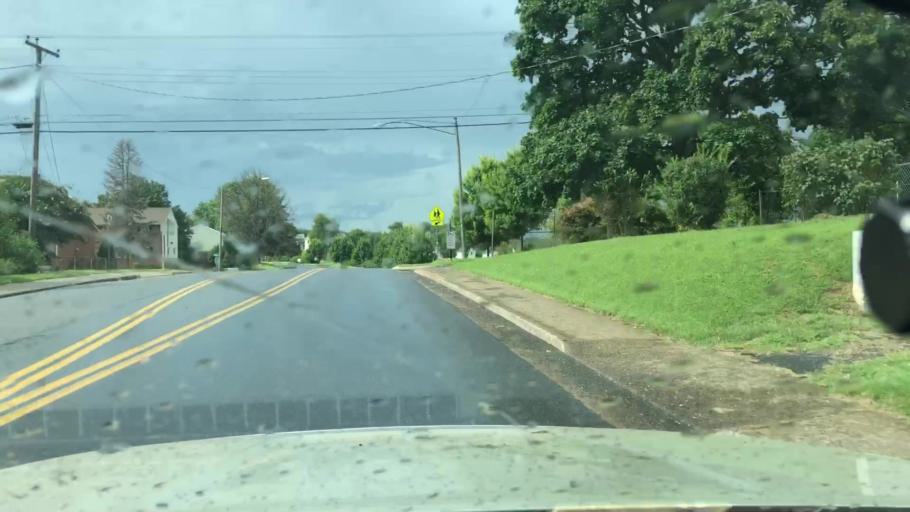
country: US
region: Virginia
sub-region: City of Waynesboro
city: Waynesboro
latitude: 38.0794
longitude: -78.8957
